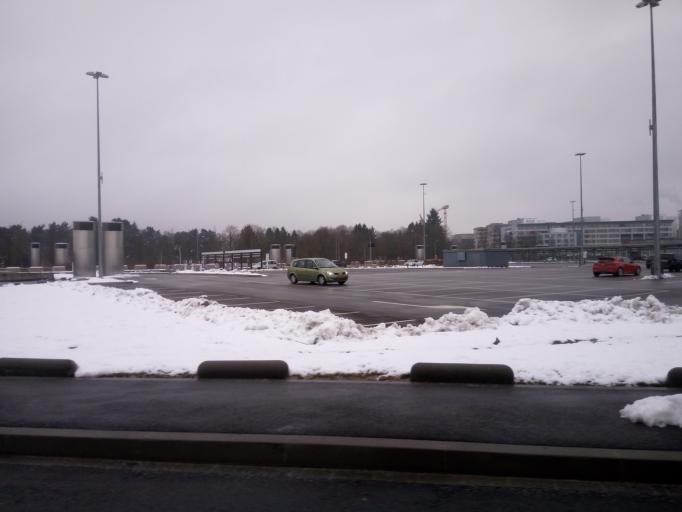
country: LU
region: Luxembourg
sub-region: Canton de Luxembourg
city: Sandweiler
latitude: 49.6346
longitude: 6.2144
